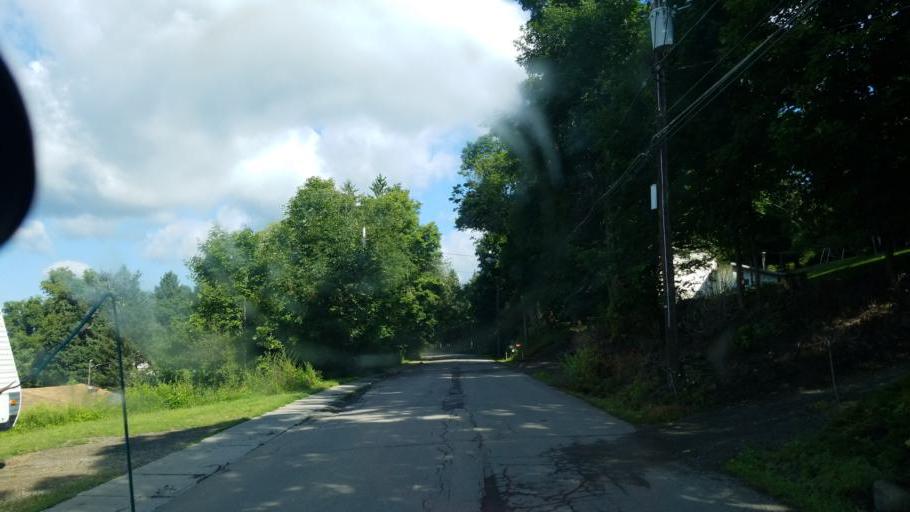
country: US
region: New York
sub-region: Steuben County
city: Canisteo
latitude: 42.2780
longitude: -77.6008
